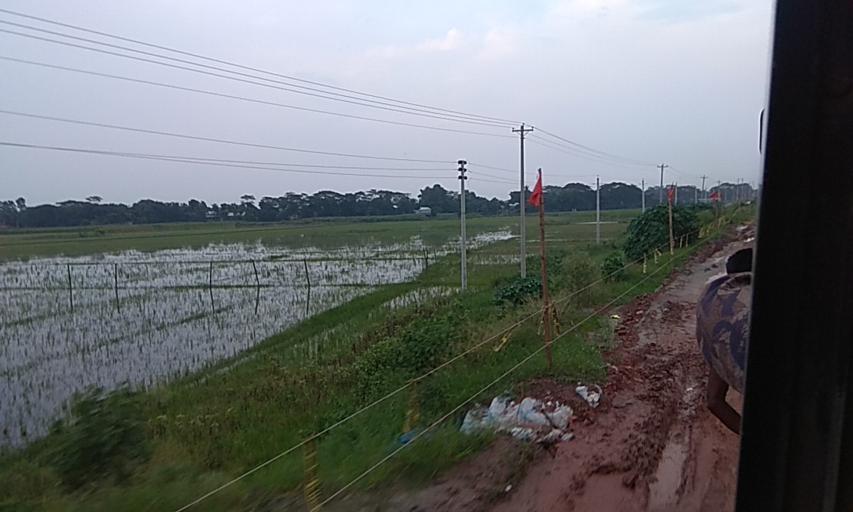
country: BD
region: Dhaka
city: Char Bhadrasan
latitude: 23.3828
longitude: 90.0008
